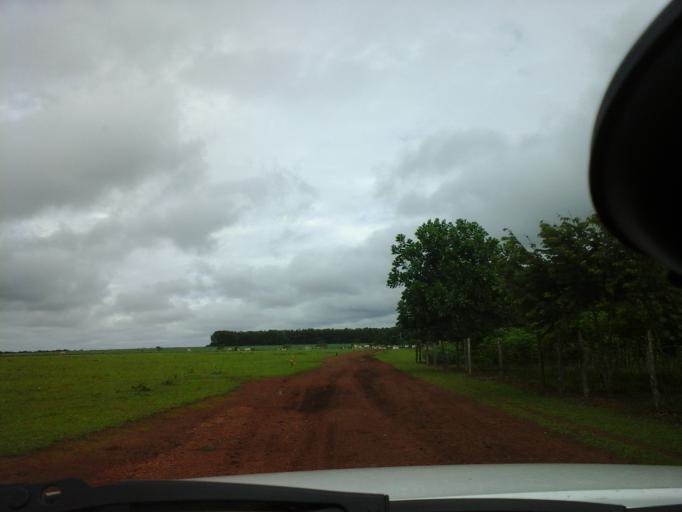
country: CO
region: Cundinamarca
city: Tibacuy
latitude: 4.2039
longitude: -72.4643
